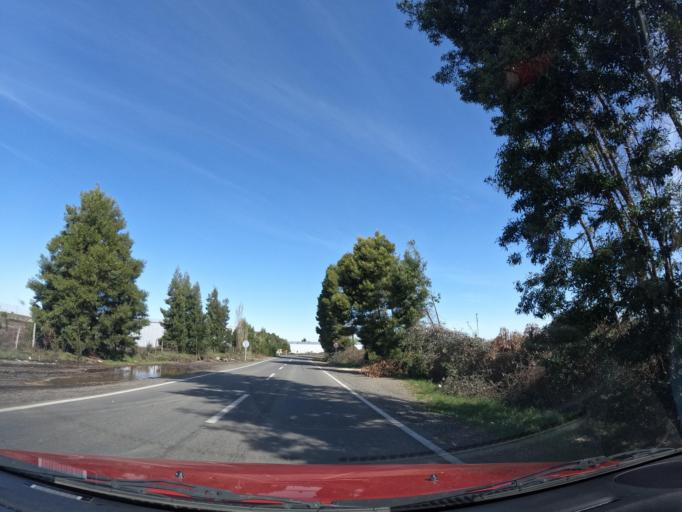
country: CL
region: Biobio
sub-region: Provincia de Biobio
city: Cabrero
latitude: -37.0384
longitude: -72.3734
